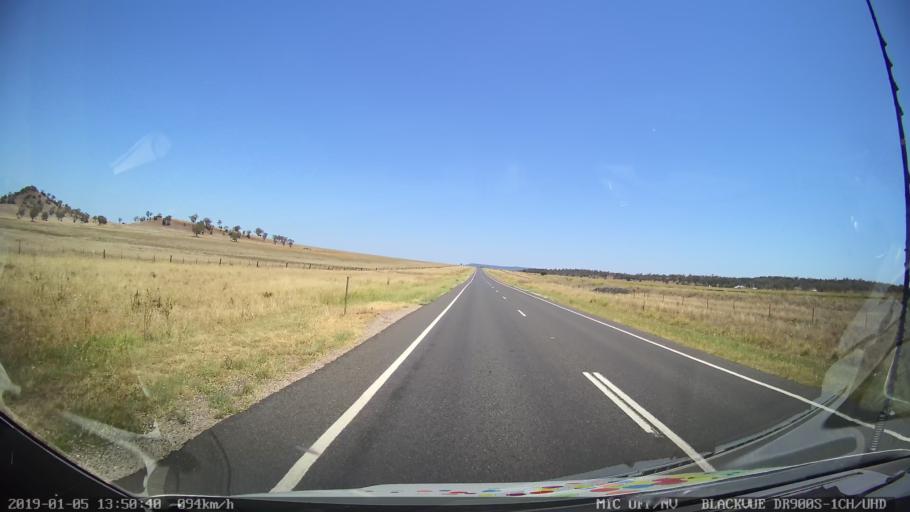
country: AU
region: New South Wales
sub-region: Gunnedah
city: Gunnedah
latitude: -31.0333
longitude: 150.2754
